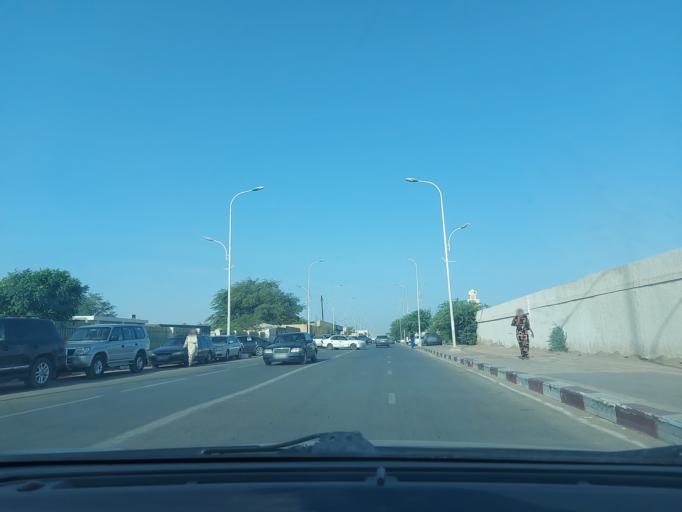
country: MR
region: Nouakchott
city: Nouakchott
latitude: 18.0863
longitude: -15.9878
